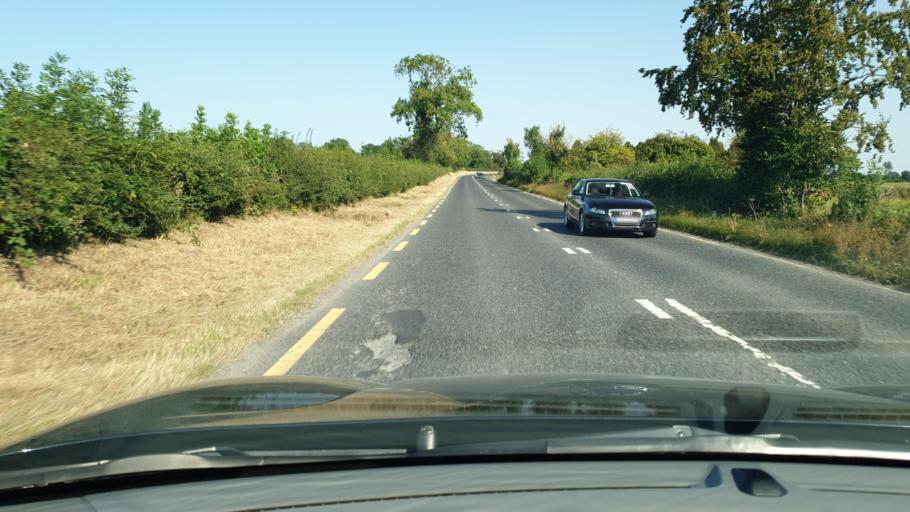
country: IE
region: Leinster
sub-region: An Mhi
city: Navan
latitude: 53.6432
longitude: -6.6266
